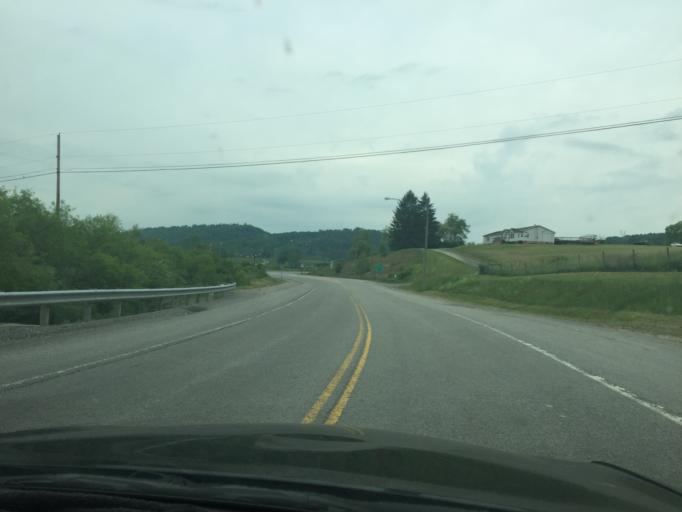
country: US
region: West Virginia
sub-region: Randolph County
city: Elkins
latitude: 39.0136
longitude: -79.8115
